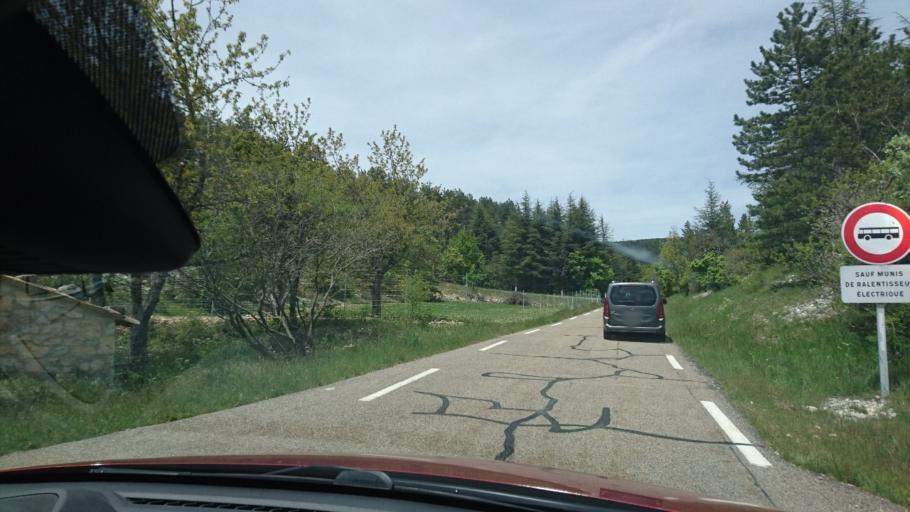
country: FR
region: Provence-Alpes-Cote d'Azur
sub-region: Departement du Vaucluse
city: Sault
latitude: 44.1355
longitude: 5.3741
